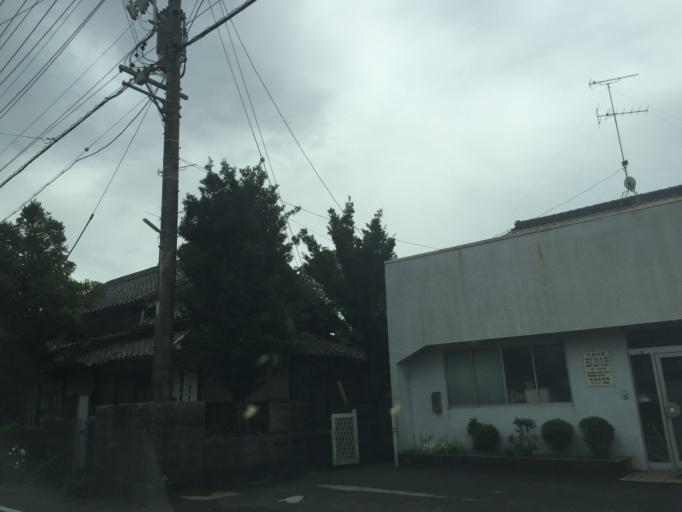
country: JP
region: Shizuoka
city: Kakegawa
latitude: 34.7701
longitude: 137.9813
